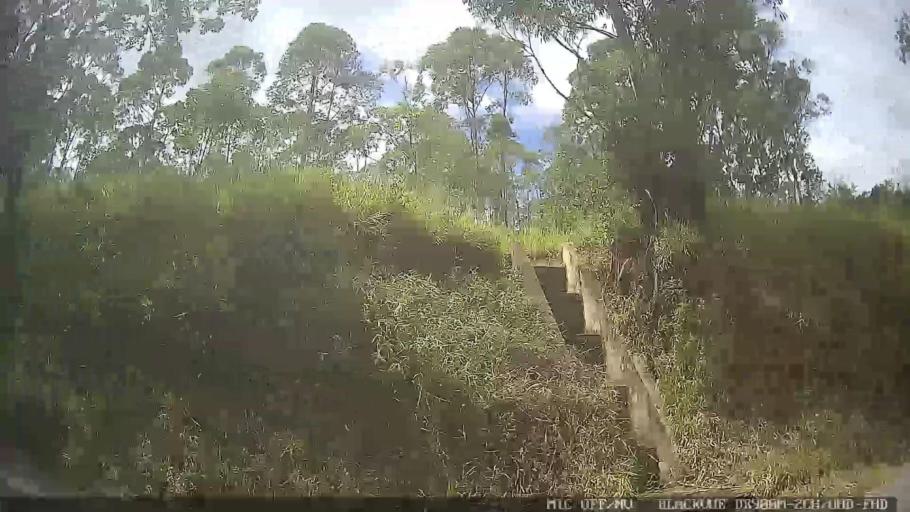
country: BR
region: Sao Paulo
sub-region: Braganca Paulista
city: Braganca Paulista
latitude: -22.8054
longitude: -46.5247
